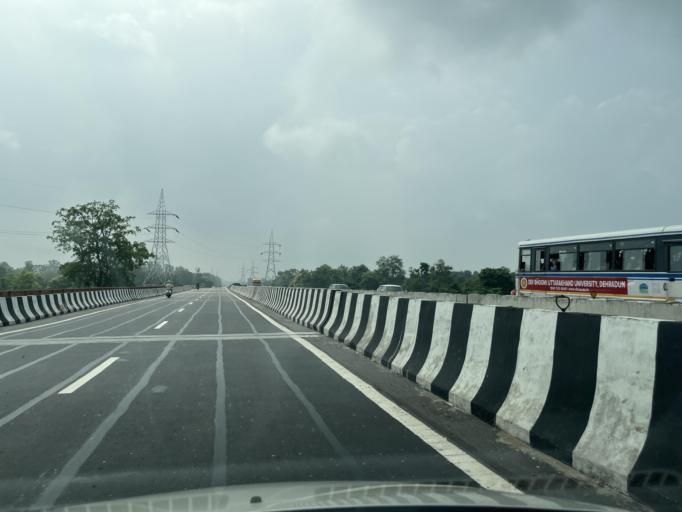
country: IN
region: Uttarakhand
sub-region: Dehradun
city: Raiwala
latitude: 30.0989
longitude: 78.1790
